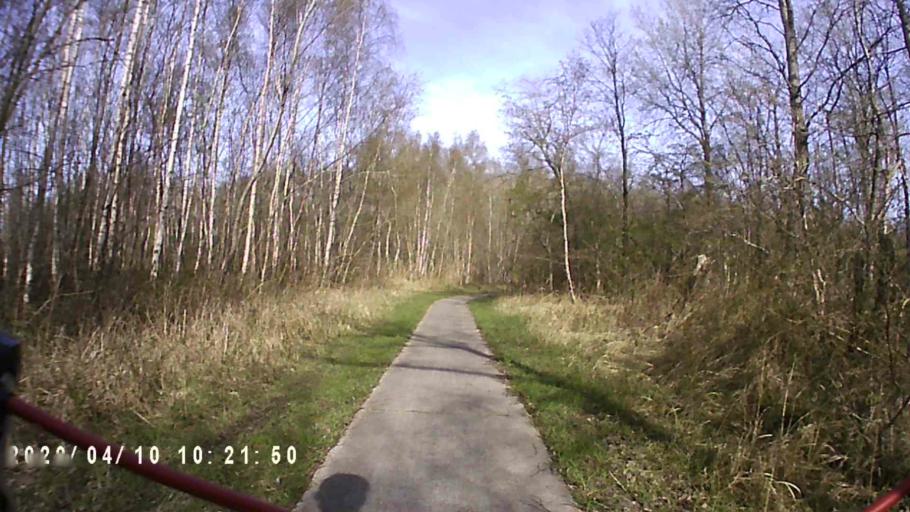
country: NL
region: Friesland
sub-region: Gemeente Dongeradeel
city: Anjum
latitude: 53.3816
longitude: 6.2159
